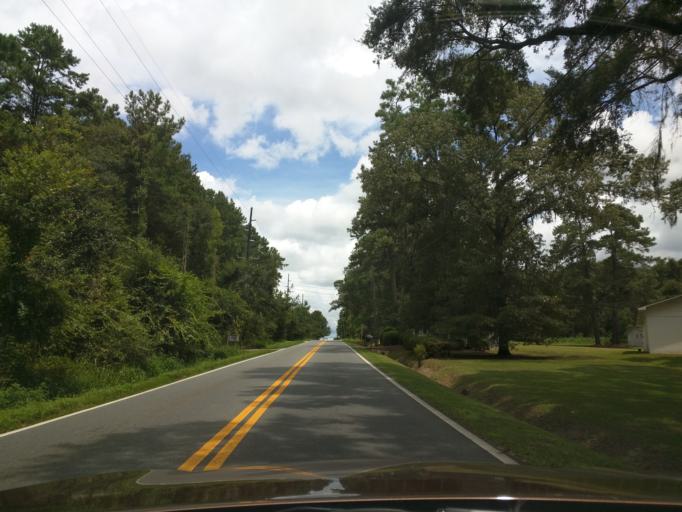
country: US
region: Florida
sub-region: Leon County
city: Tallahassee
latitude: 30.5386
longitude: -84.1764
